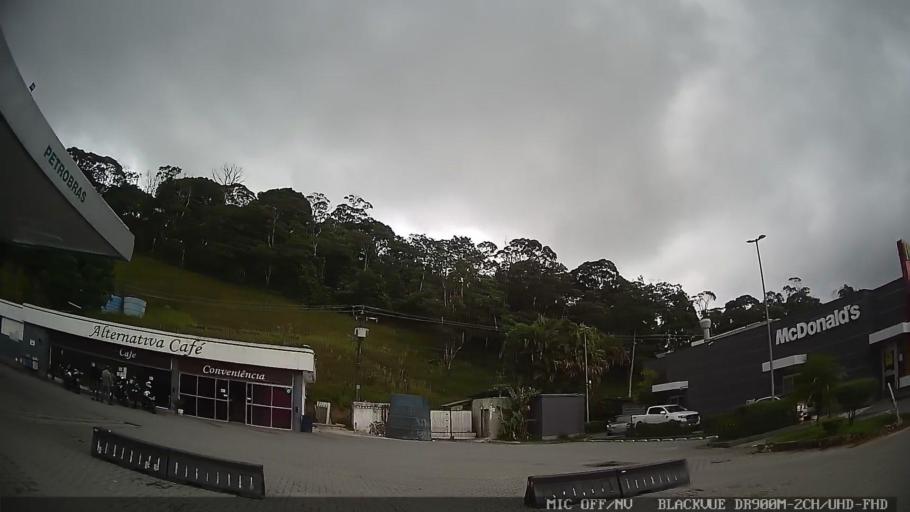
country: BR
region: Sao Paulo
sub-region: Sao Bernardo Do Campo
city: Sao Bernardo do Campo
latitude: -23.8430
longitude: -46.5757
